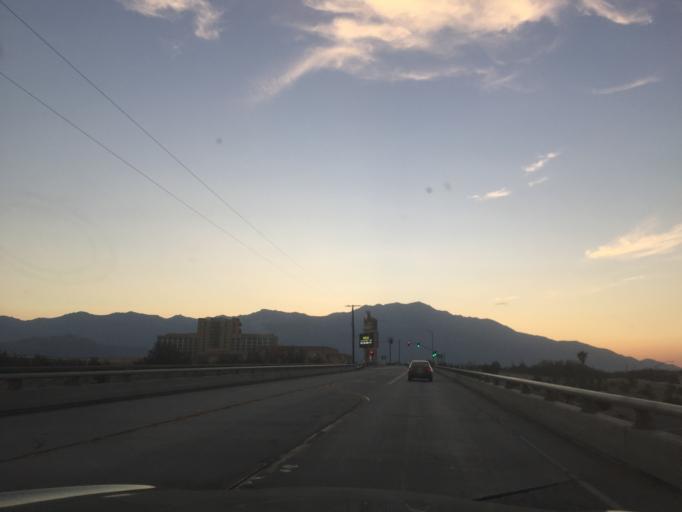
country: US
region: California
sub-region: Riverside County
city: Thousand Palms
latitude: 33.8164
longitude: -116.4033
